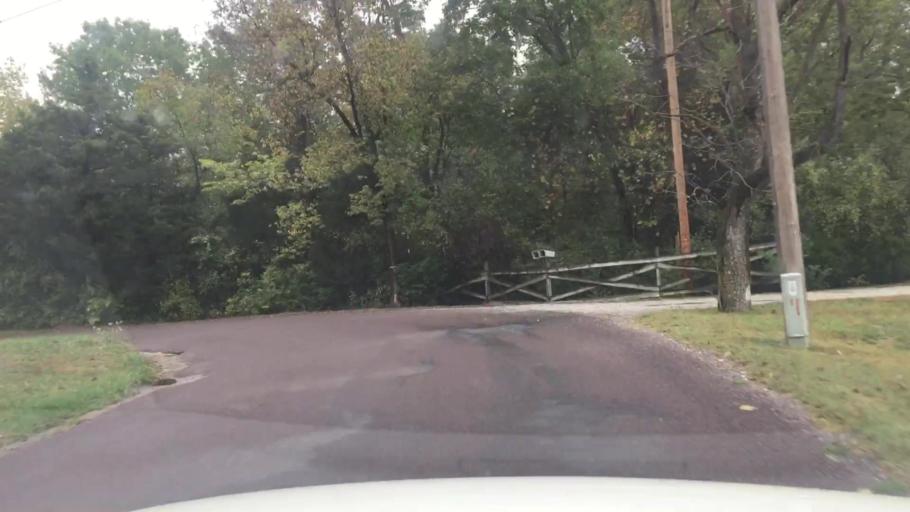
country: US
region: Missouri
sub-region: Boone County
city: Columbia
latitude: 38.8559
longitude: -92.3502
